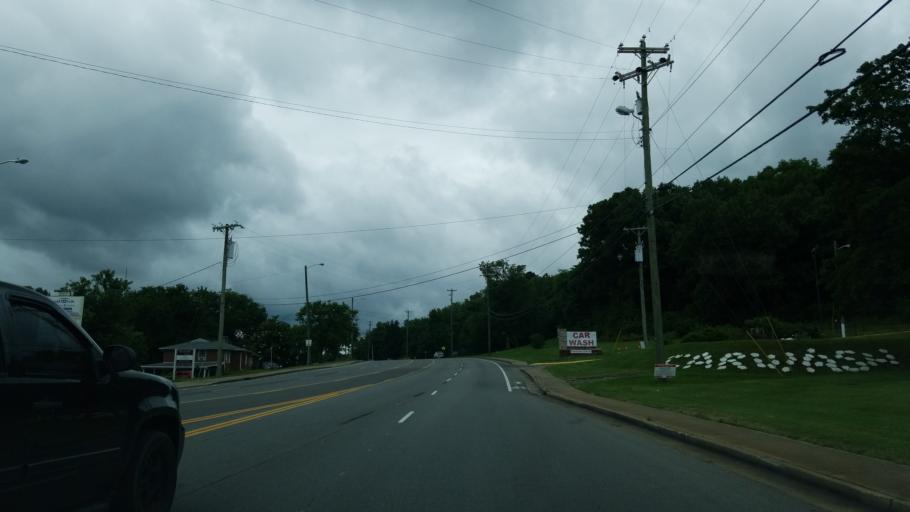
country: US
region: Tennessee
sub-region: Rutherford County
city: La Vergne
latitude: 36.0706
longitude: -86.6368
